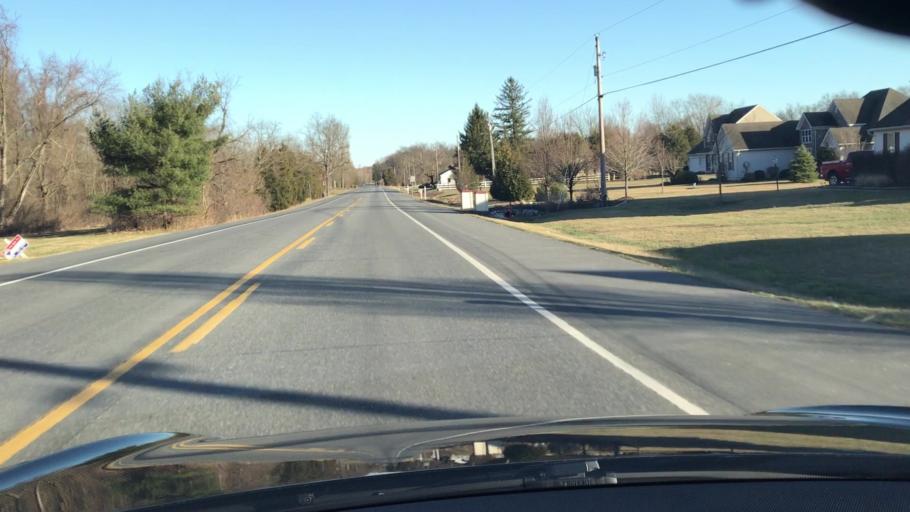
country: US
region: Pennsylvania
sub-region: York County
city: Valley Green
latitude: 40.1444
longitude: -76.8755
